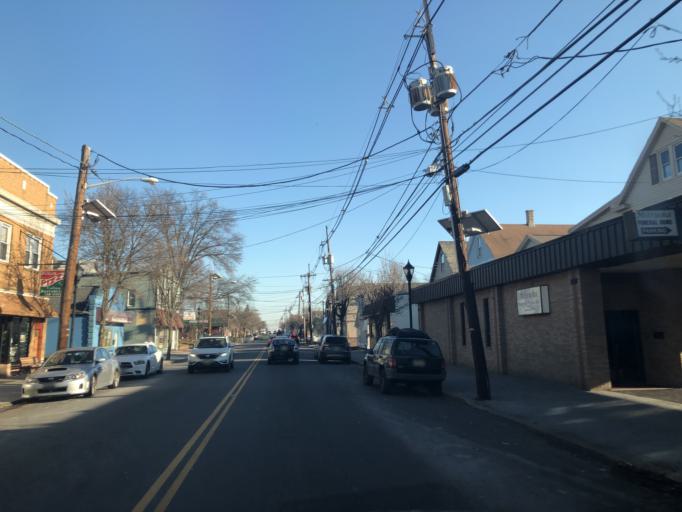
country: US
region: New Jersey
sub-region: Middlesex County
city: Fords
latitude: 40.5283
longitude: -74.3138
